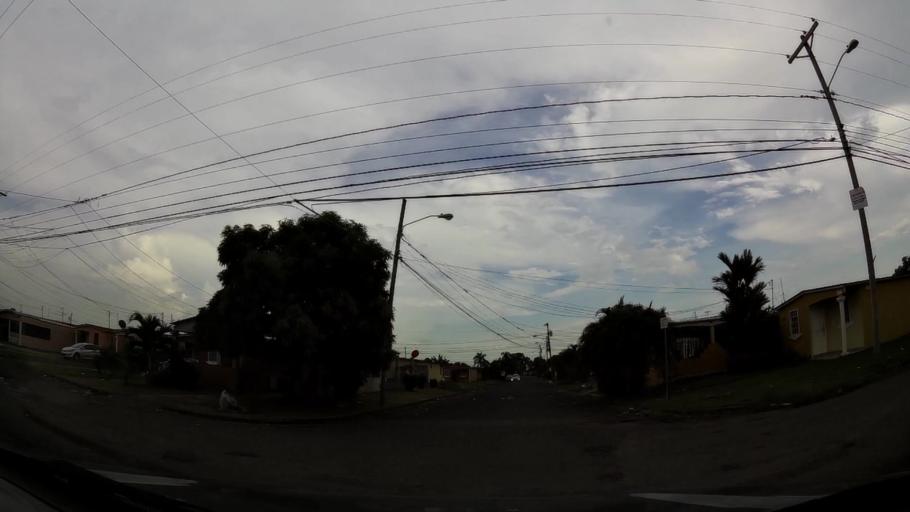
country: PA
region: Panama
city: Cabra Numero Uno
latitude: 9.0864
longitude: -79.3527
